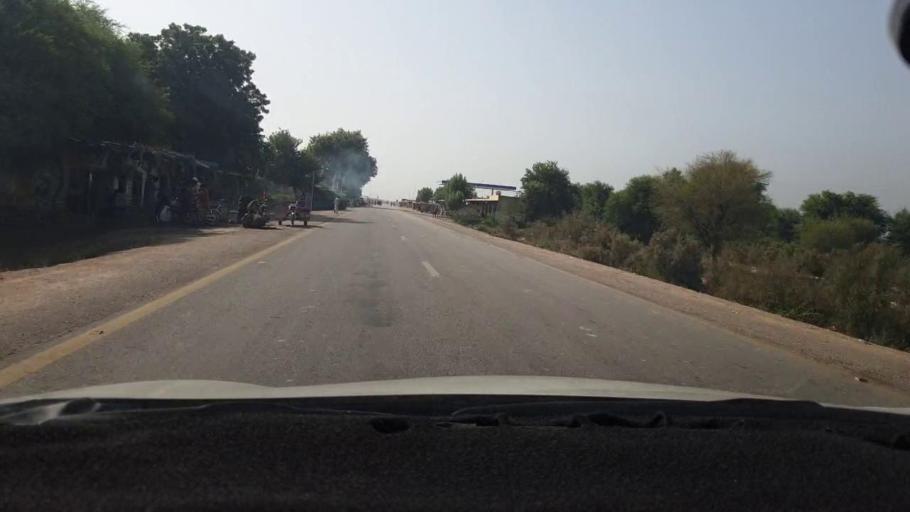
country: PK
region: Sindh
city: Sanghar
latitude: 25.9900
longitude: 68.9657
